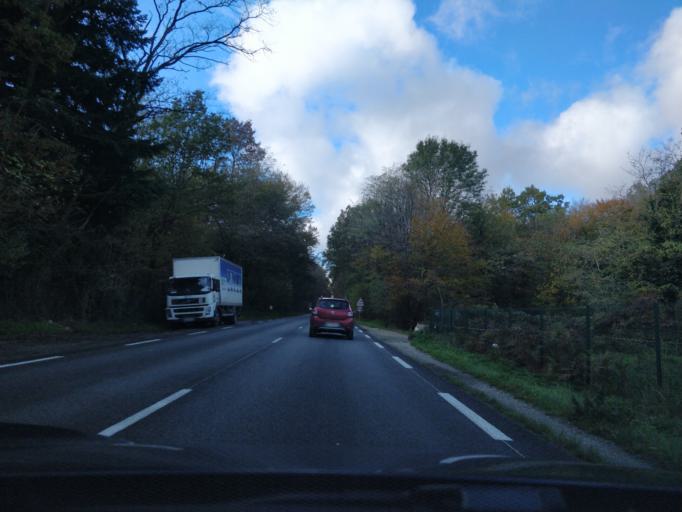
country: FR
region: Ile-de-France
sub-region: Departement de l'Essonne
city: Bruyeres-le-Chatel
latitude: 48.6070
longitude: 2.1937
